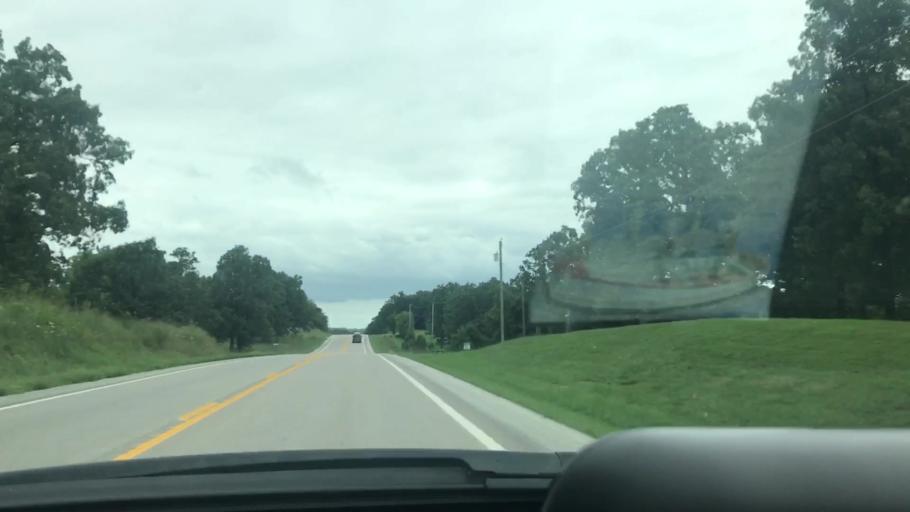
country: US
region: Missouri
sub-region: Dallas County
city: Buffalo
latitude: 37.7107
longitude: -93.1147
